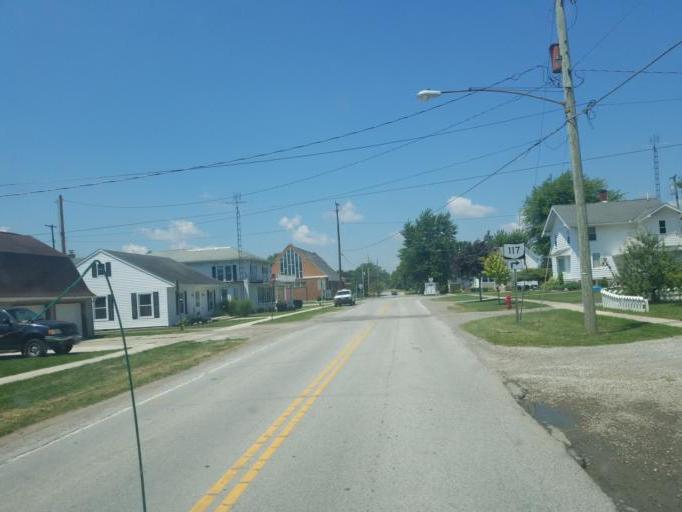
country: US
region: Ohio
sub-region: Allen County
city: Spencerville
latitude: 40.7091
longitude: -84.3545
